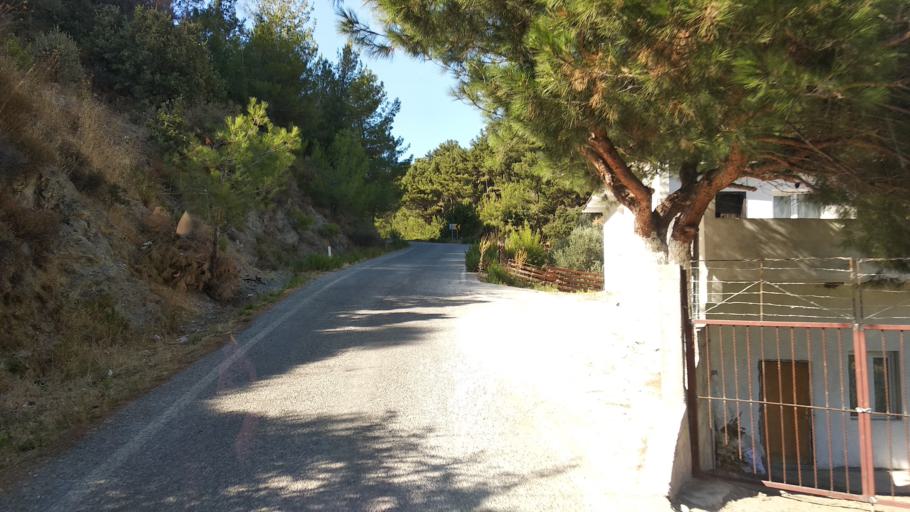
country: TR
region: Izmir
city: Gaziemir
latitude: 38.3255
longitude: 26.9568
